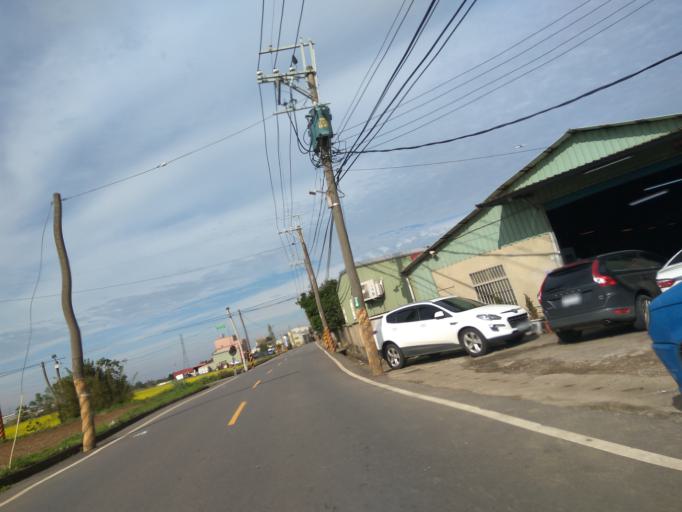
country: TW
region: Taiwan
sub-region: Hsinchu
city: Zhubei
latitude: 24.9523
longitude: 121.1298
